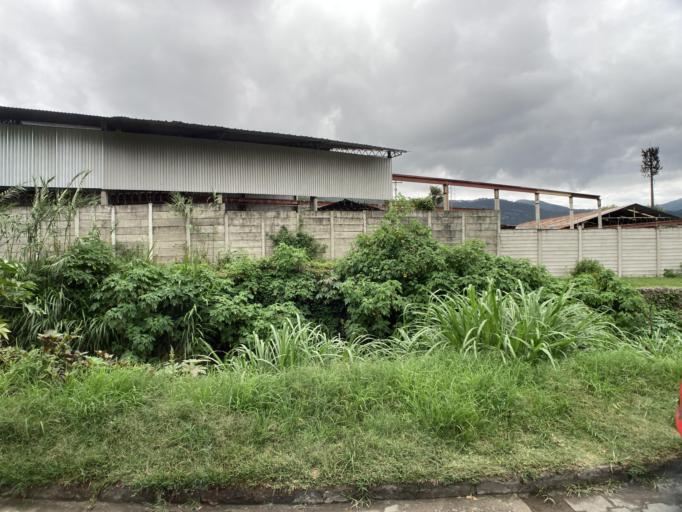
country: GT
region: Sacatepequez
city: Jocotenango
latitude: 14.5828
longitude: -90.7489
